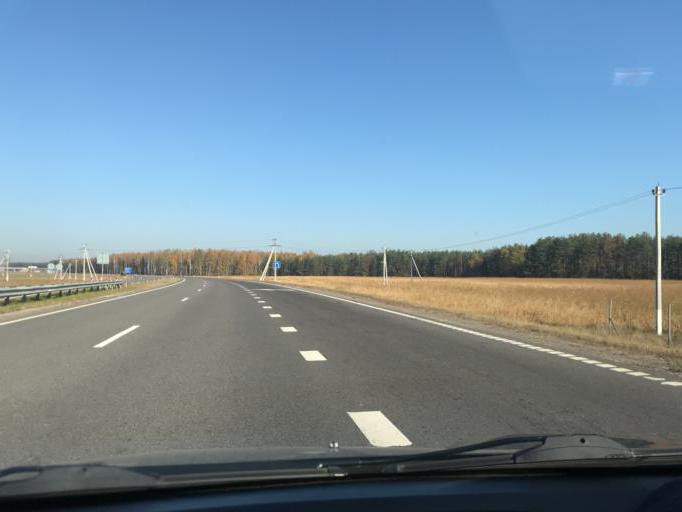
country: BY
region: Mogilev
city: Babruysk
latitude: 53.1297
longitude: 29.3656
